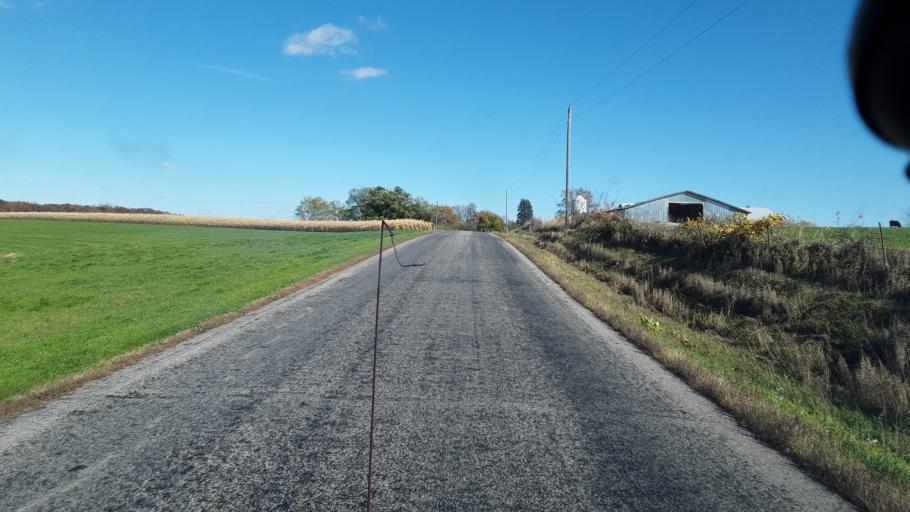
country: US
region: Wisconsin
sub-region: Vernon County
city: Hillsboro
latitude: 43.6863
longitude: -90.4116
